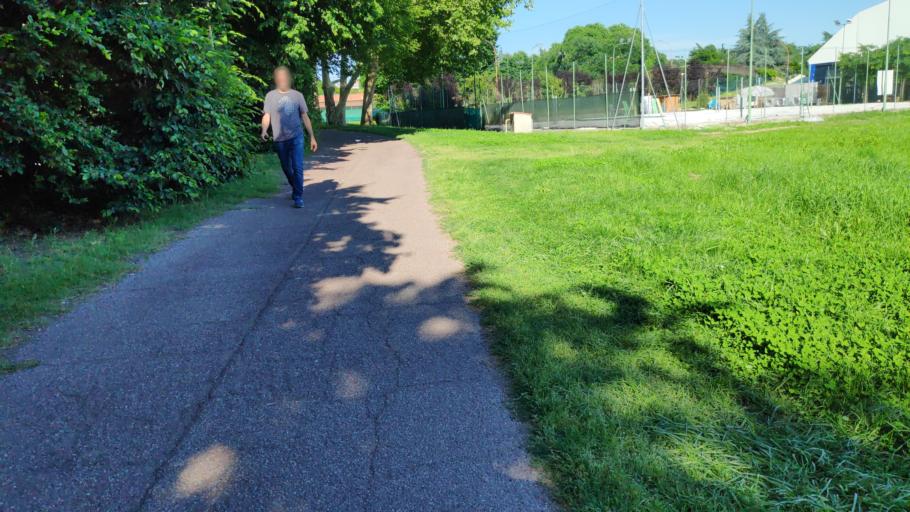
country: IT
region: Lombardy
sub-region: Citta metropolitana di Milano
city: Basiglio
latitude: 45.3575
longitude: 9.1550
